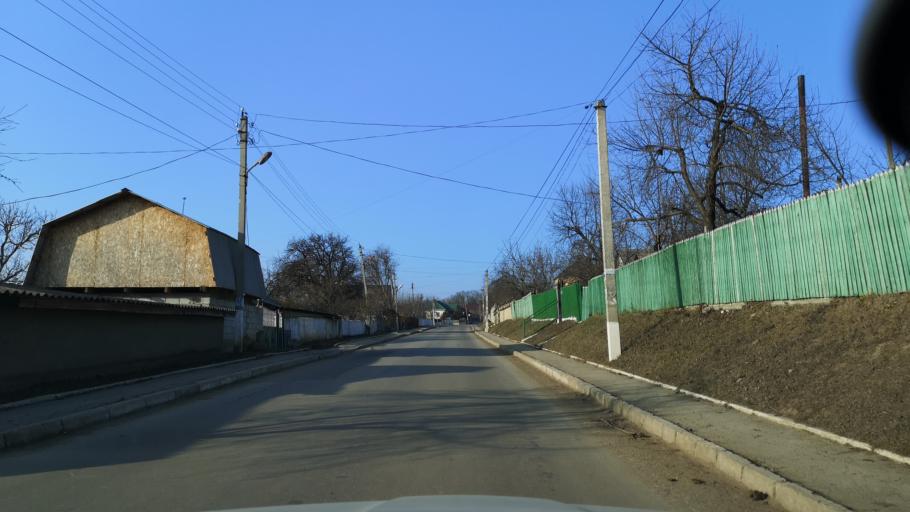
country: MD
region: Stinga Nistrului
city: Bucovat
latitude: 47.1138
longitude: 28.5081
